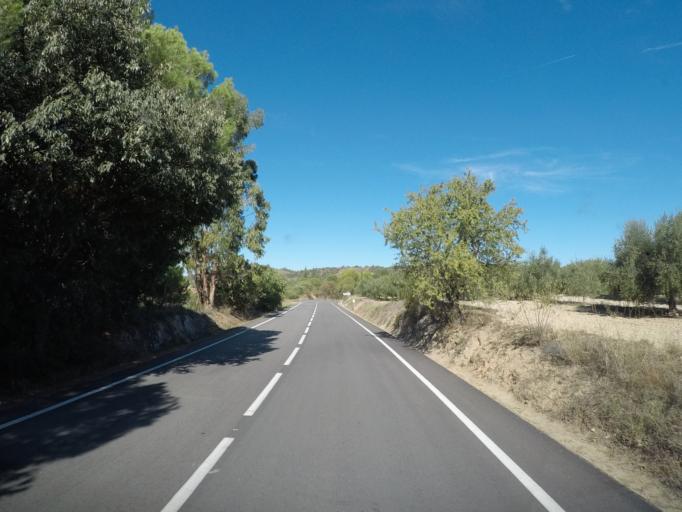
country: ES
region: Catalonia
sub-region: Provincia de Tarragona
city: Falset
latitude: 41.1537
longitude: 0.8176
